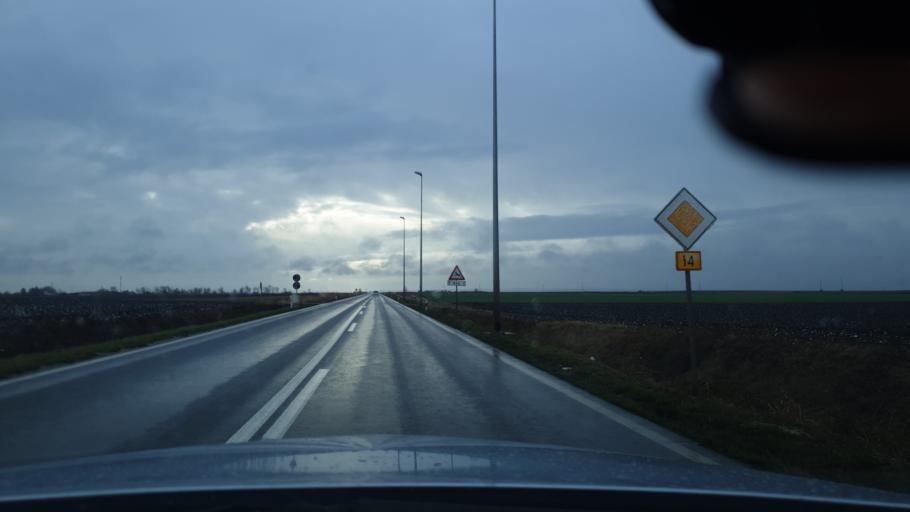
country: RS
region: Autonomna Pokrajina Vojvodina
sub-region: Juznobanatski Okrug
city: Kovin
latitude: 44.8226
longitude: 20.8521
